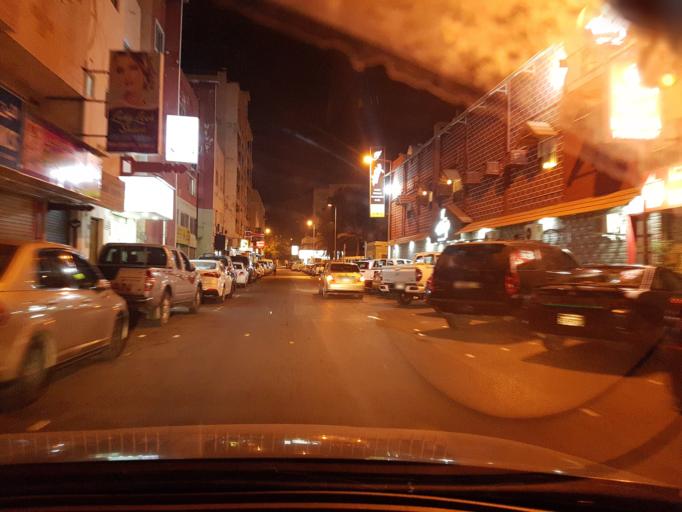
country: BH
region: Manama
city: Manama
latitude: 26.2274
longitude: 50.5858
